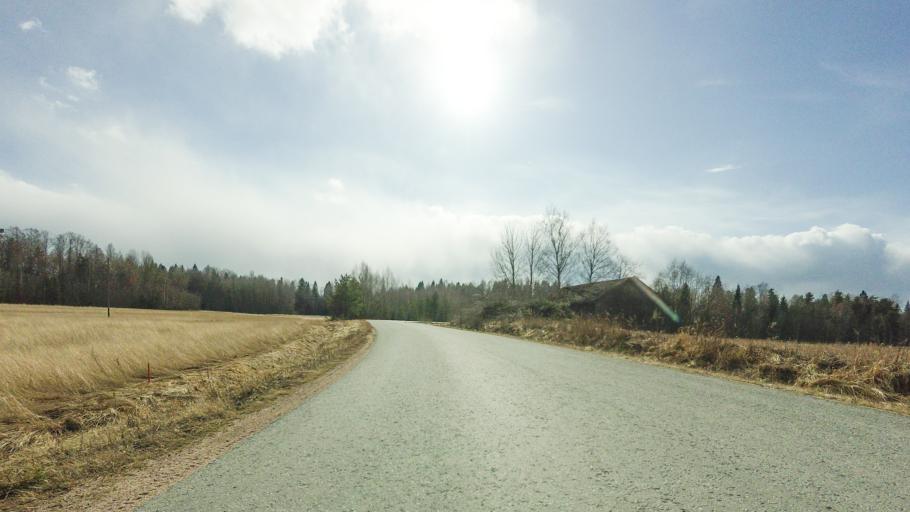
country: FI
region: Varsinais-Suomi
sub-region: Salo
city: Suomusjaervi
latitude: 60.3451
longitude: 23.6833
